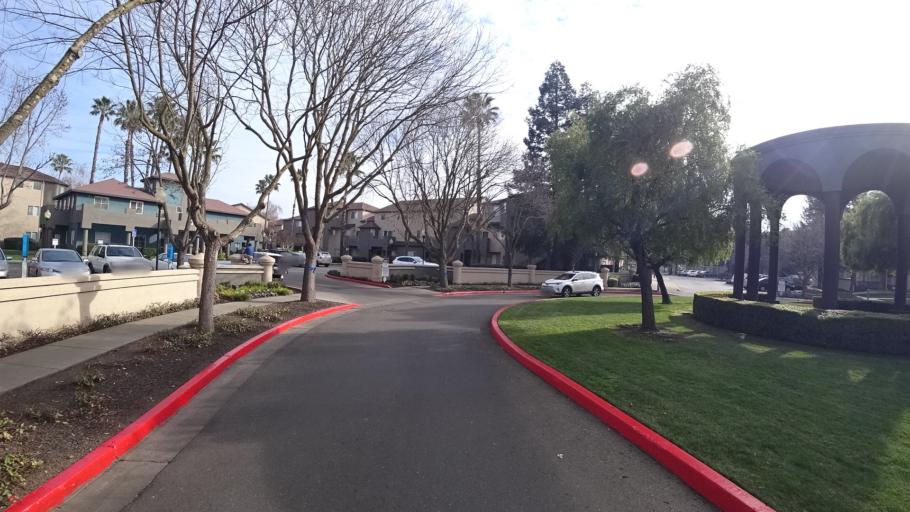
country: US
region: California
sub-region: Yolo County
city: Davis
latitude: 38.5377
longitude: -121.7268
